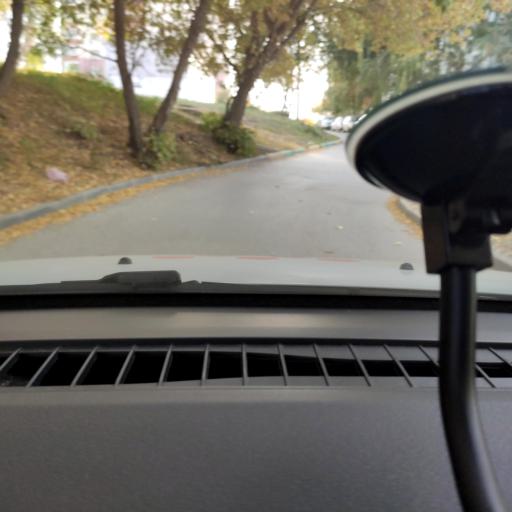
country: RU
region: Samara
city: Samara
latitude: 53.1920
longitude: 50.1486
